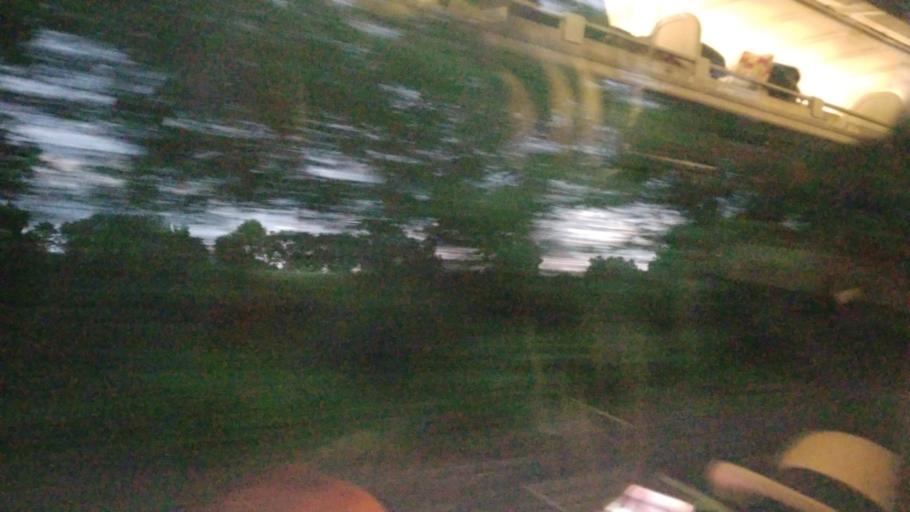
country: US
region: Virginia
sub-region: Orange County
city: Gordonsville
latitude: 38.2094
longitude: -78.2163
